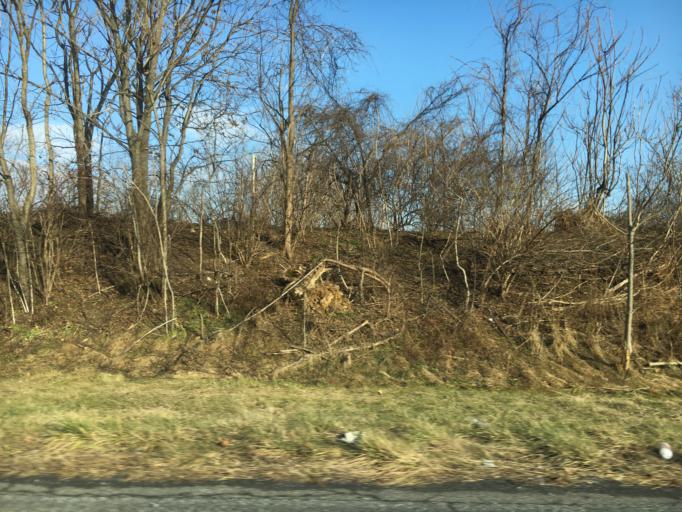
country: US
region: Pennsylvania
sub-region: Lehigh County
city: Stiles
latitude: 40.6682
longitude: -75.5136
